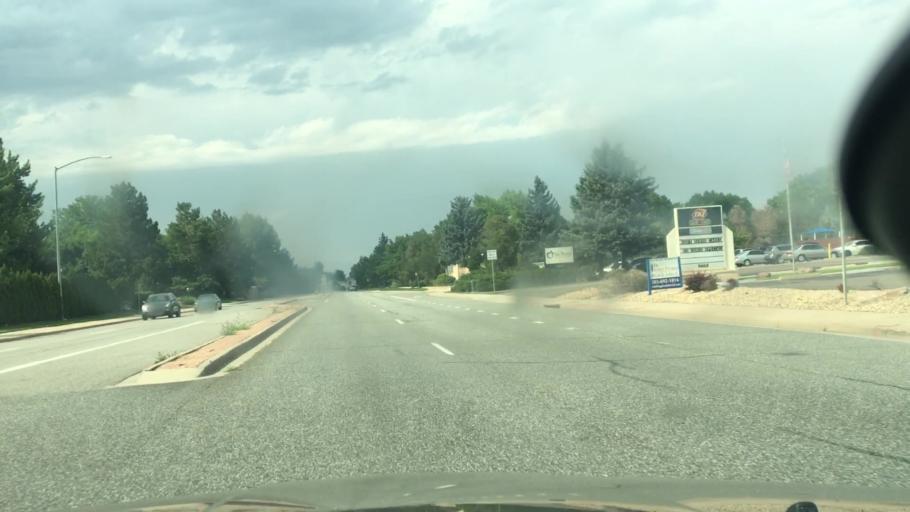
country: US
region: Colorado
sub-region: Arapahoe County
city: Castlewood
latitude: 39.6325
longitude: -104.8852
